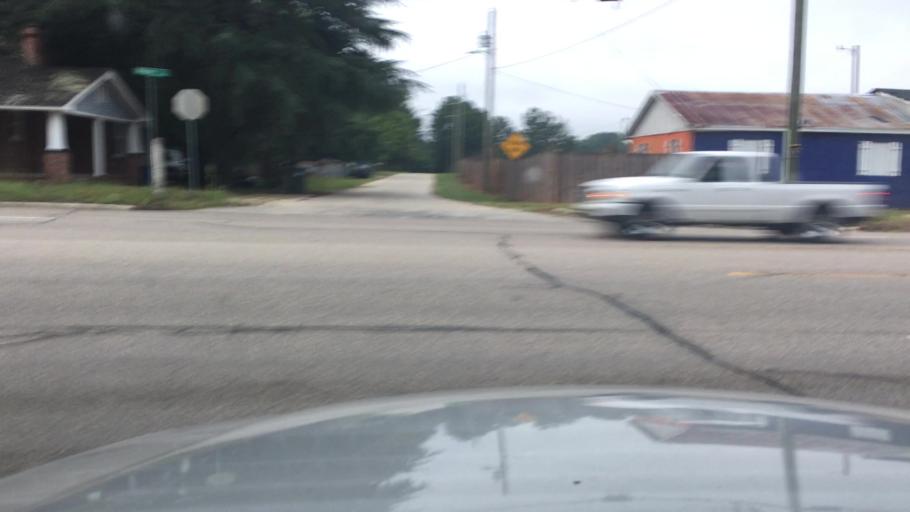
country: US
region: North Carolina
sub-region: Cumberland County
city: Fayetteville
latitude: 35.0273
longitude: -78.8909
